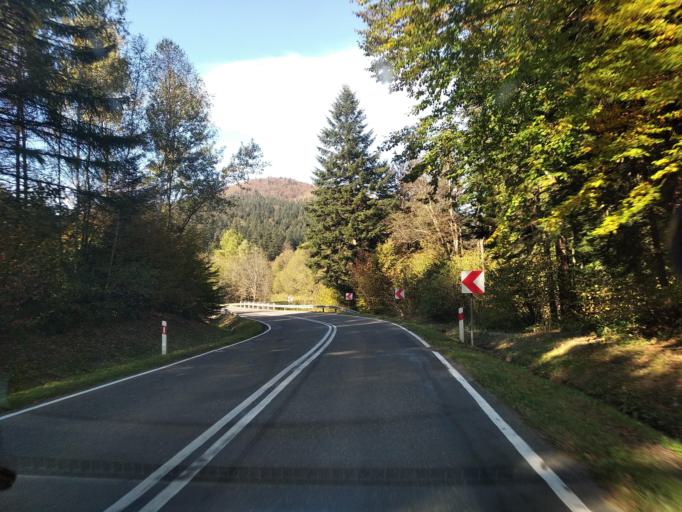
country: PL
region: Subcarpathian Voivodeship
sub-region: Powiat leski
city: Baligrod
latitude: 49.2904
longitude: 22.2701
